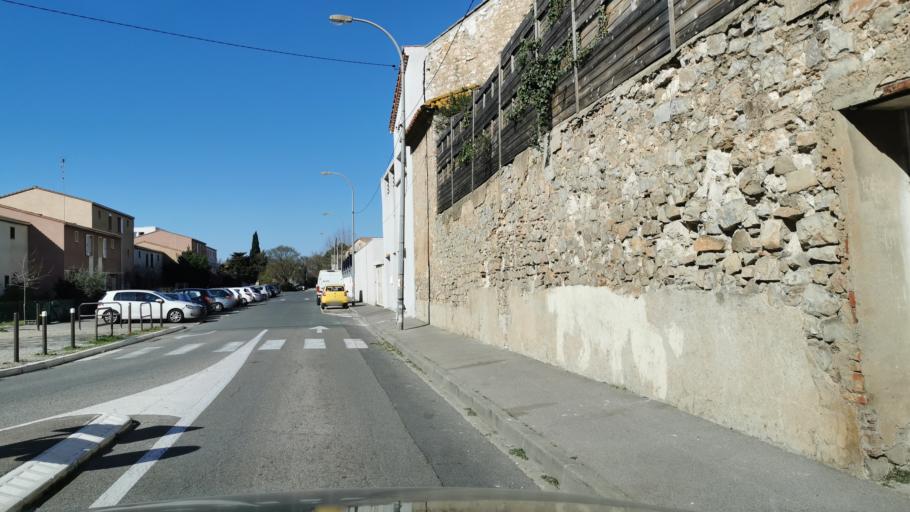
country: FR
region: Languedoc-Roussillon
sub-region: Departement de l'Aude
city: Narbonne
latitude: 43.1888
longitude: 2.9960
